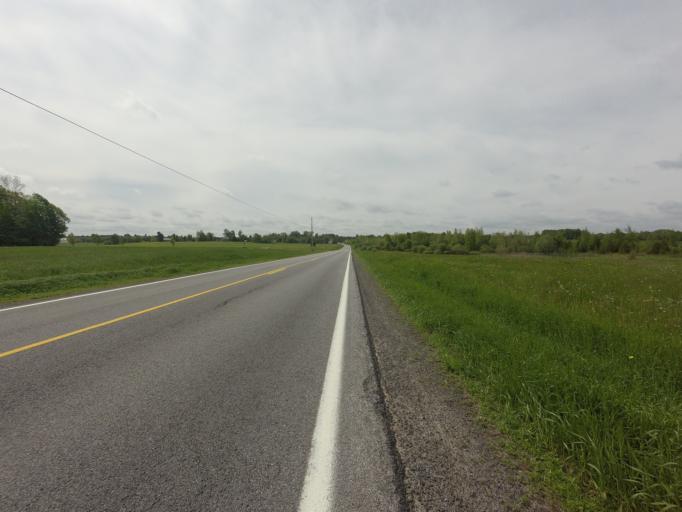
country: CA
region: Ontario
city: Cornwall
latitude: 44.7048
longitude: -74.6594
